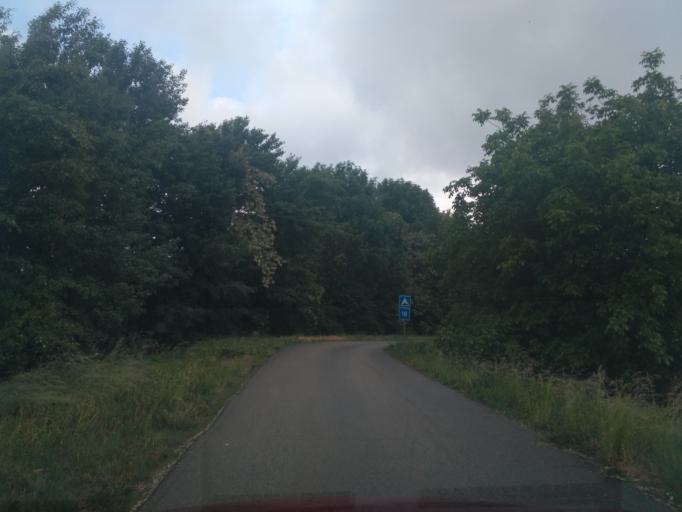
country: SK
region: Kosicky
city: Moldava nad Bodvou
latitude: 48.6868
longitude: 21.0746
